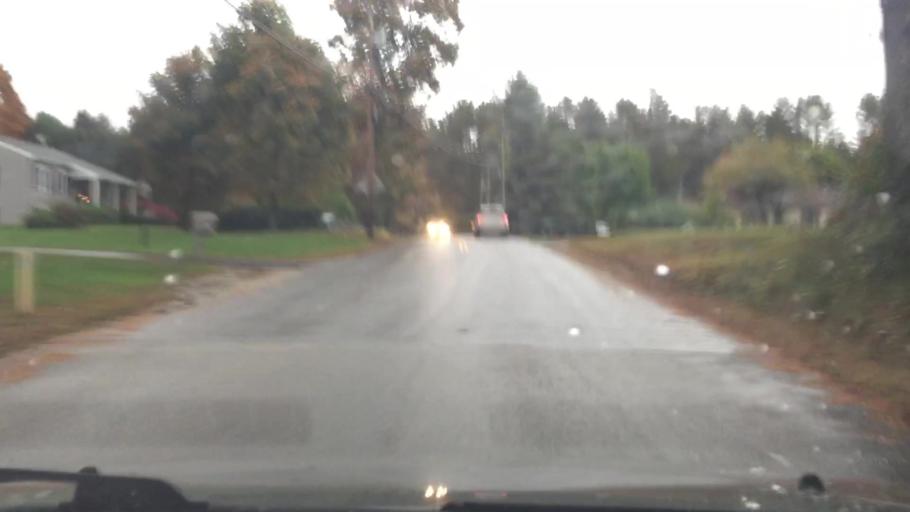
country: US
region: New Hampshire
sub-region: Cheshire County
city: Swanzey
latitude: 42.8861
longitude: -72.2862
